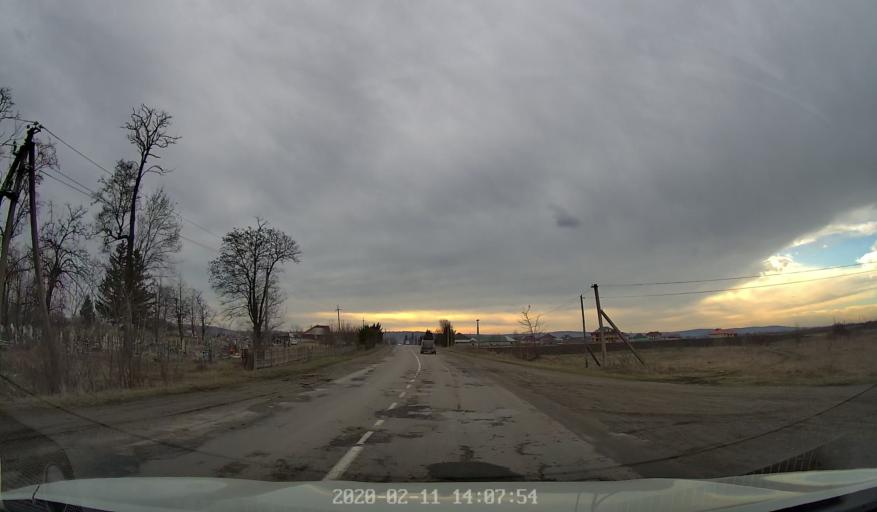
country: RO
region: Botosani
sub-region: Comuna Darabani
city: Bajura
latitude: 48.2426
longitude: 26.5487
